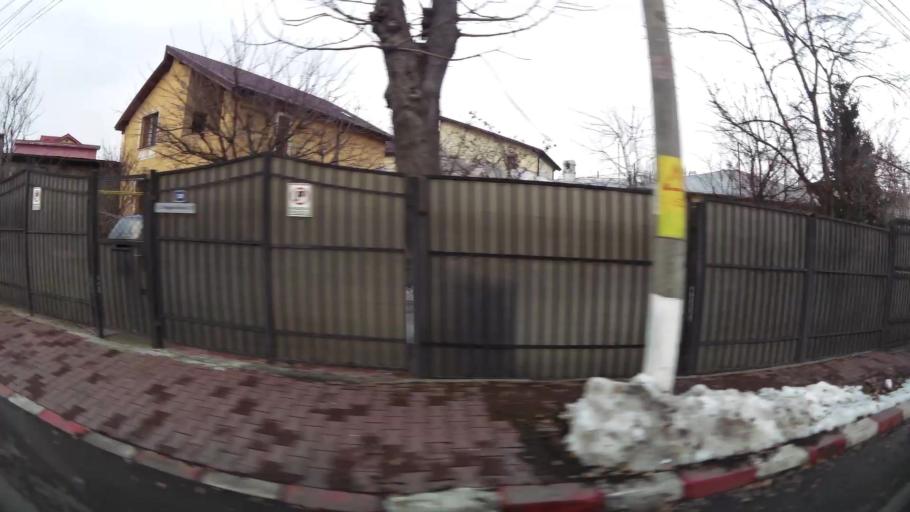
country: RO
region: Ilfov
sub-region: Voluntari City
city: Voluntari
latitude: 44.4815
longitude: 26.1789
